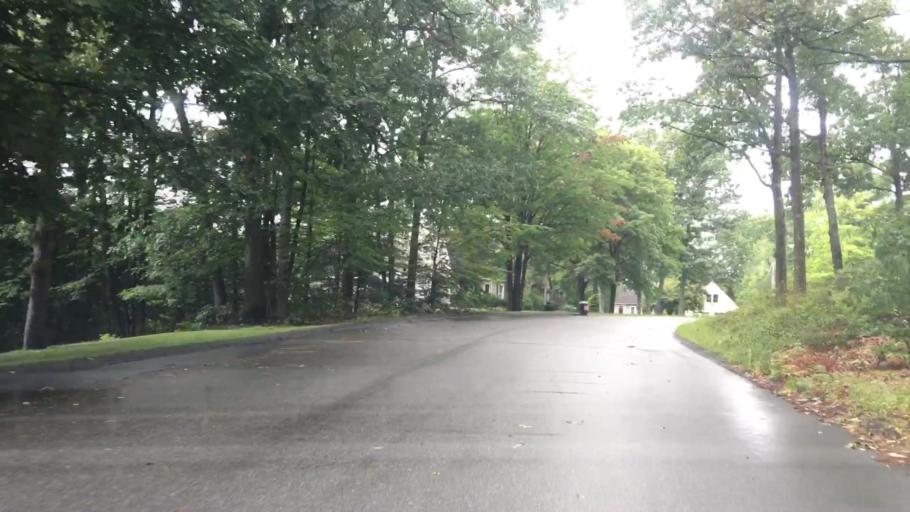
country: US
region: Maine
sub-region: York County
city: South Sanford
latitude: 43.4199
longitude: -70.7620
